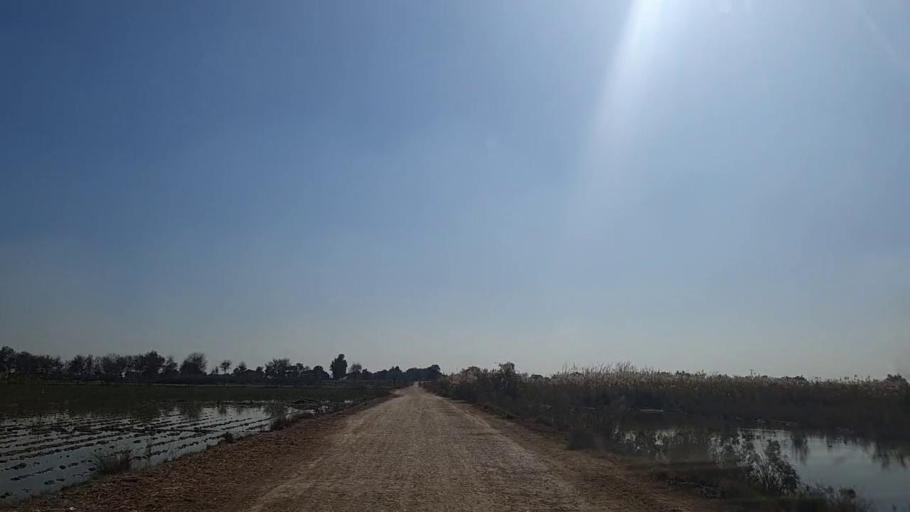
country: PK
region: Sindh
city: Sakrand
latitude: 26.2494
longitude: 68.1936
